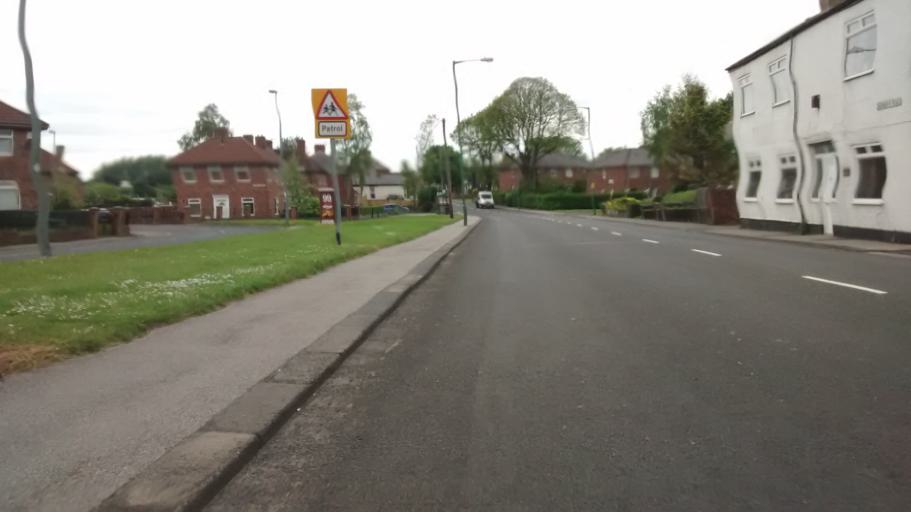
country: GB
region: England
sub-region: County Durham
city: Durham
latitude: 54.7774
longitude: -1.5473
